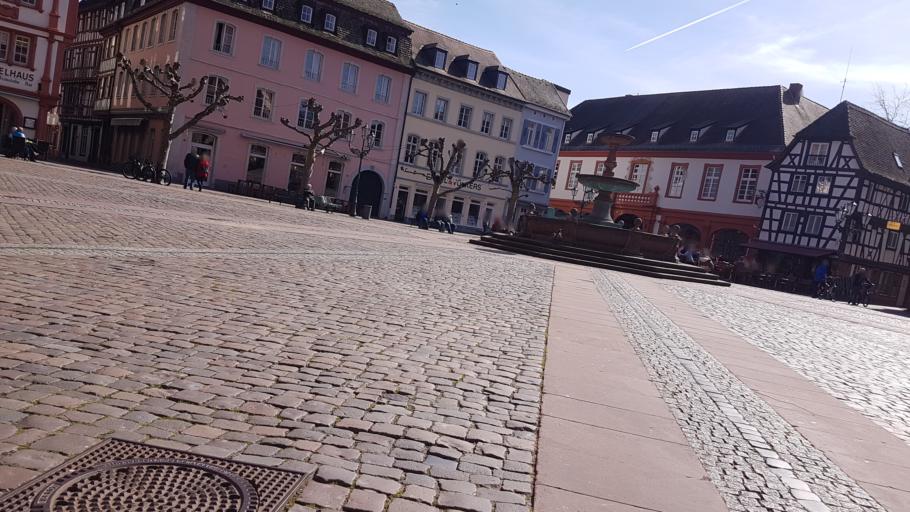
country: DE
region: Rheinland-Pfalz
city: Neustadt
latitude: 49.3538
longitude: 8.1359
